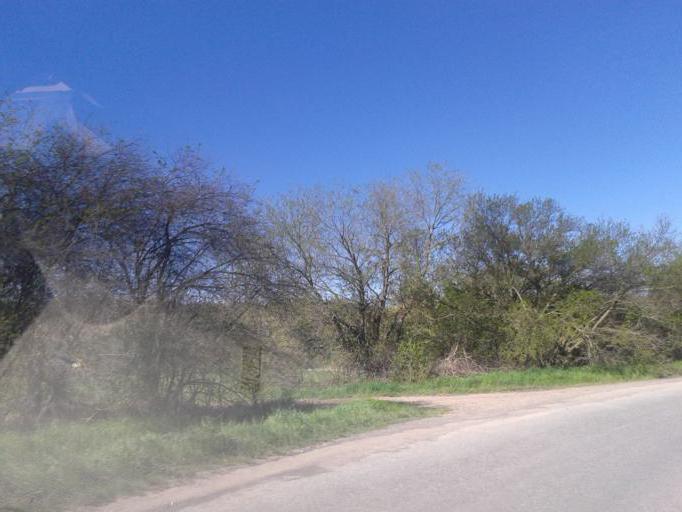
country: CZ
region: Central Bohemia
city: Revnice
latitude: 49.8822
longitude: 14.1477
